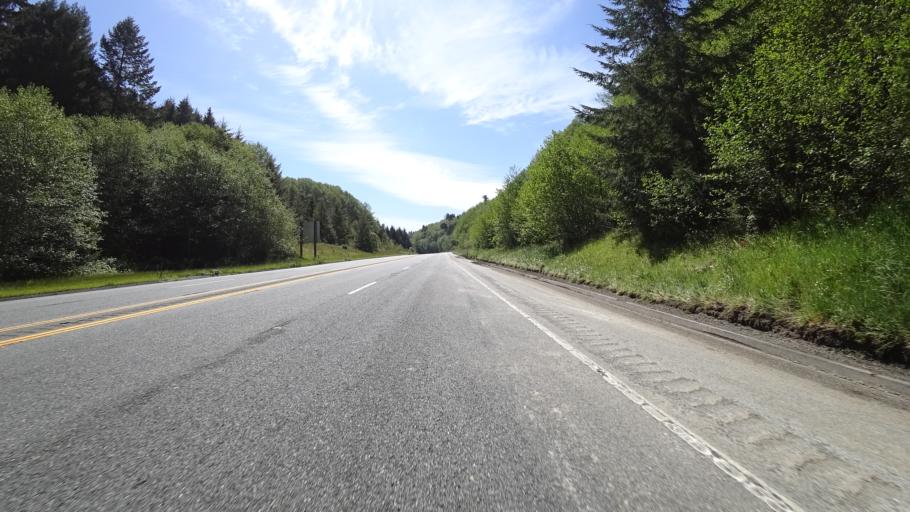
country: US
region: California
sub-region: Del Norte County
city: Bertsch-Oceanview
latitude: 41.4631
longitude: -124.0362
